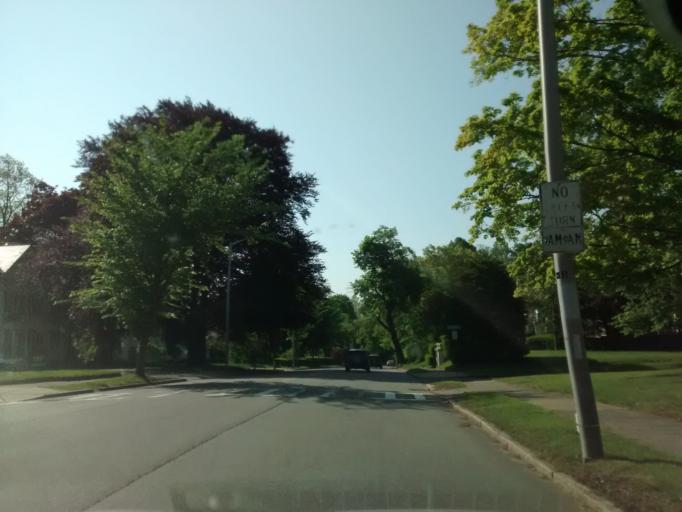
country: US
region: Massachusetts
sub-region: Worcester County
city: Worcester
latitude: 42.2811
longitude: -71.8129
